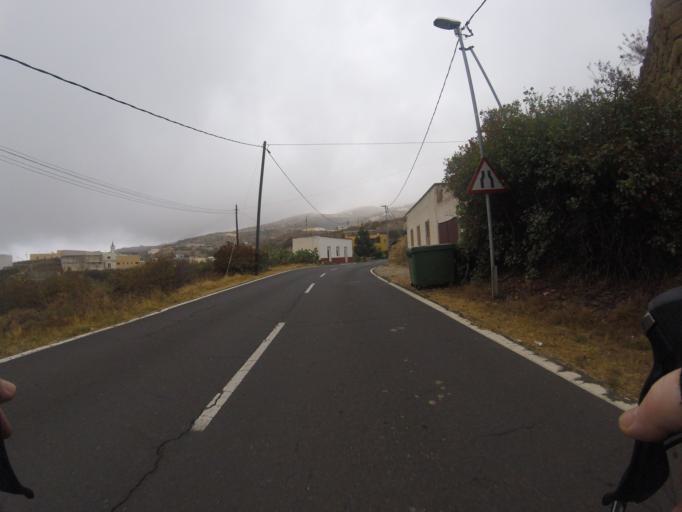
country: ES
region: Canary Islands
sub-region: Provincia de Santa Cruz de Tenerife
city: Guimar
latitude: 28.2812
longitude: -16.4072
